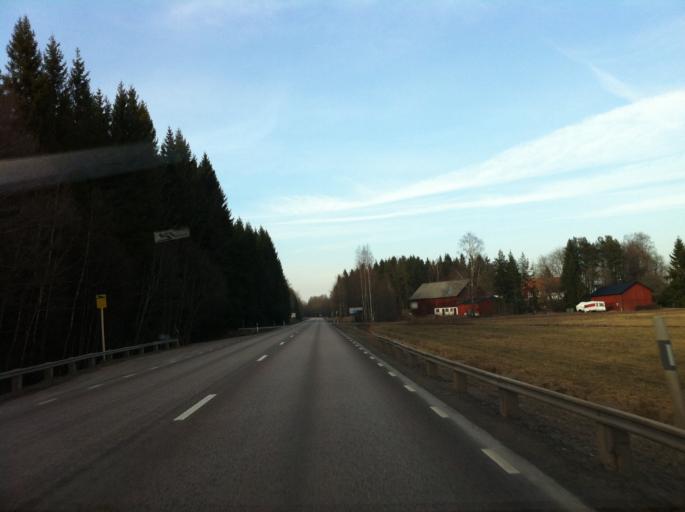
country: SE
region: Vaermland
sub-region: Storfors Kommun
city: Storfors
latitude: 59.5822
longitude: 14.2582
